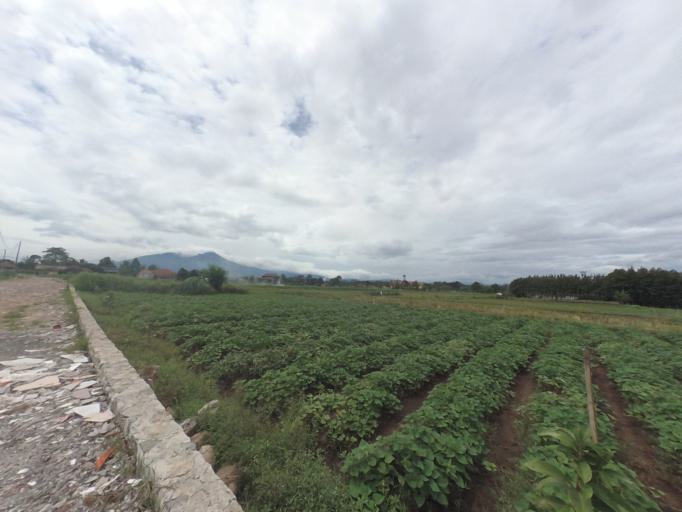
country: ID
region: West Java
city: Ciampea
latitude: -6.5493
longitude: 106.7395
